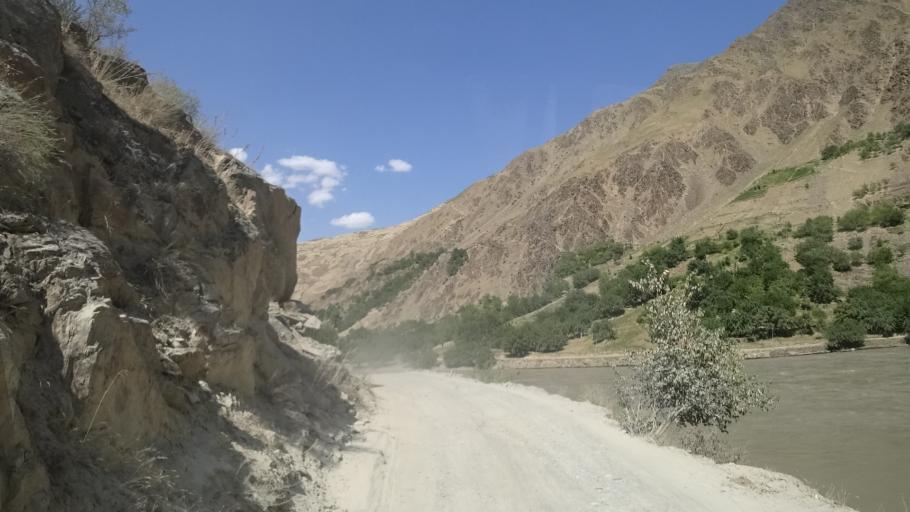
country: AF
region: Badakhshan
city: Maymay
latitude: 38.4420
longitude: 70.9569
